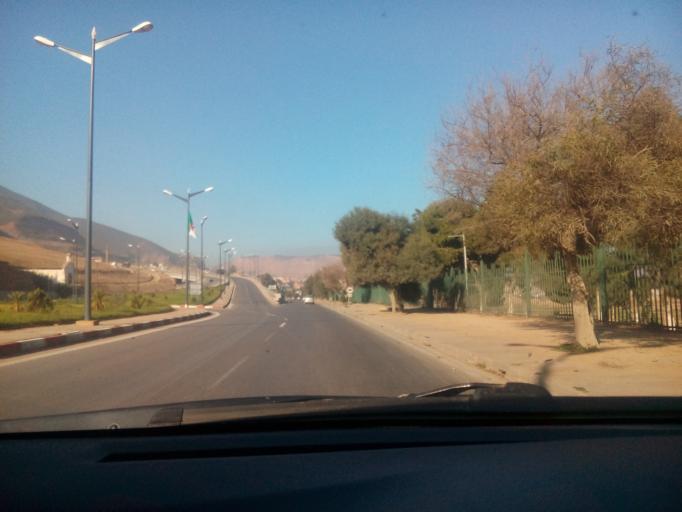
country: DZ
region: Oran
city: Mers el Kebir
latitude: 35.7142
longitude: -0.6886
